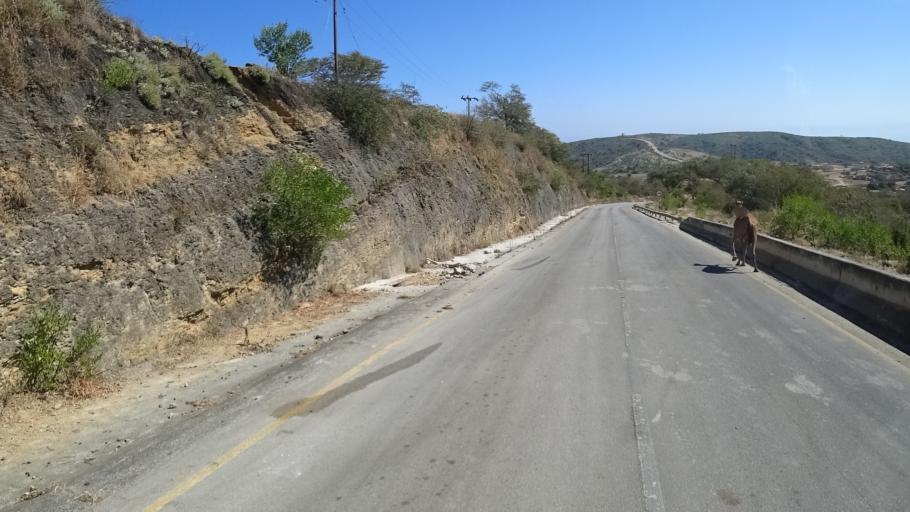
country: YE
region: Al Mahrah
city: Hawf
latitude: 16.7625
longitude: 53.3388
